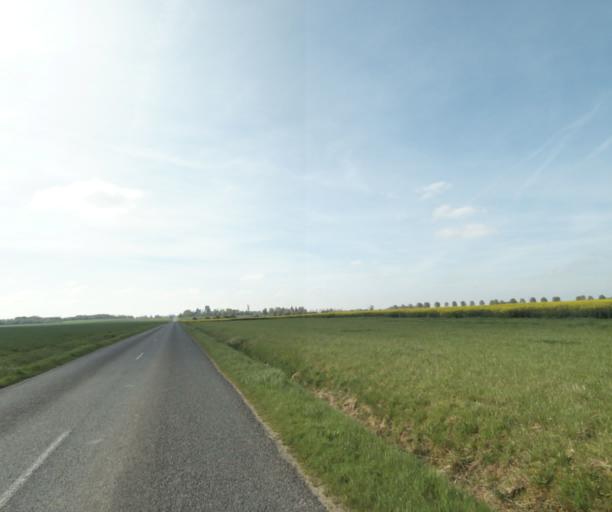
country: FR
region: Ile-de-France
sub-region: Departement de Seine-et-Marne
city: Nangis
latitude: 48.5763
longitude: 3.0119
